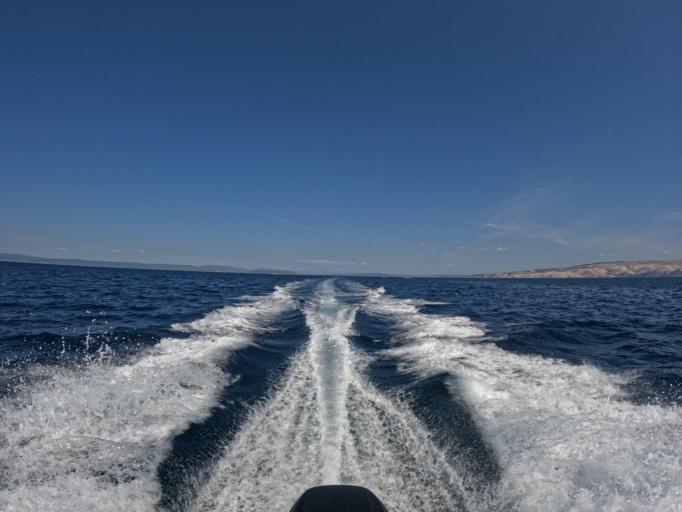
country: HR
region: Primorsko-Goranska
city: Lopar
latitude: 44.8932
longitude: 14.6426
